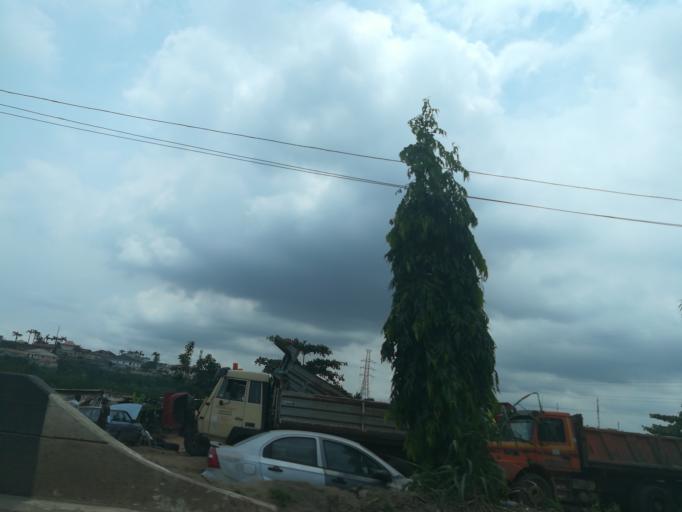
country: NG
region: Lagos
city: Ojota
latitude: 6.5807
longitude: 3.3934
